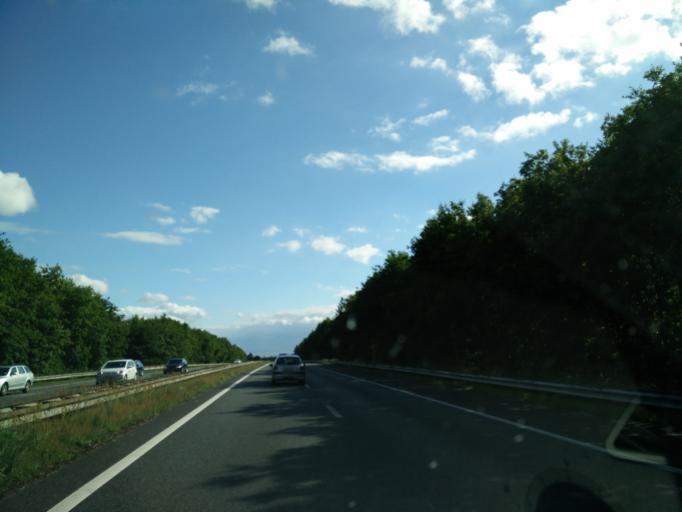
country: NL
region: Drenthe
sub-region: Gemeente Tynaarlo
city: Vries
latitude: 53.0479
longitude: 6.5907
